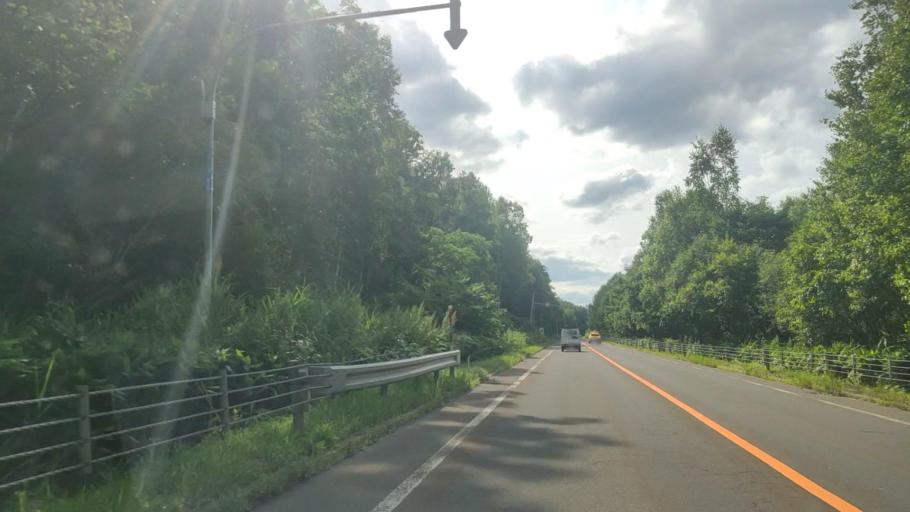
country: JP
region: Hokkaido
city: Nayoro
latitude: 44.3854
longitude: 142.4061
